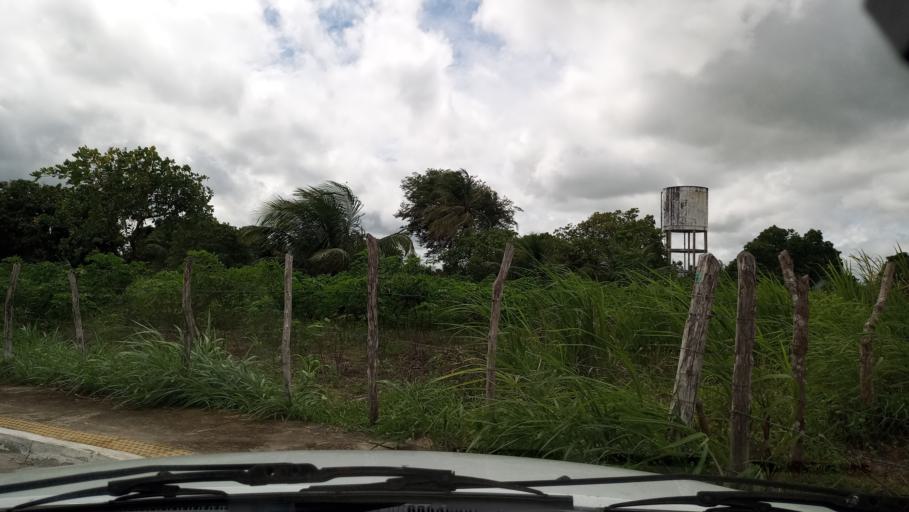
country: BR
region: Rio Grande do Norte
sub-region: Brejinho
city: Brejinho
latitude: -6.1552
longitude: -35.4362
